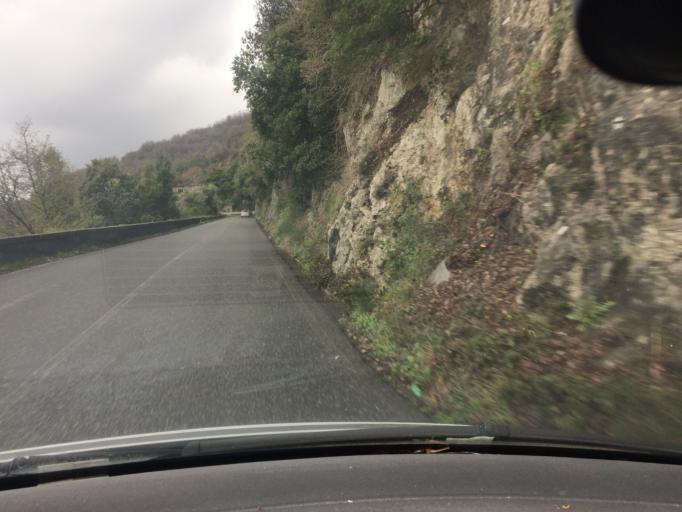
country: IT
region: Tuscany
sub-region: Provincia di Massa-Carrara
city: Massa
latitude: 44.0616
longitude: 10.1184
